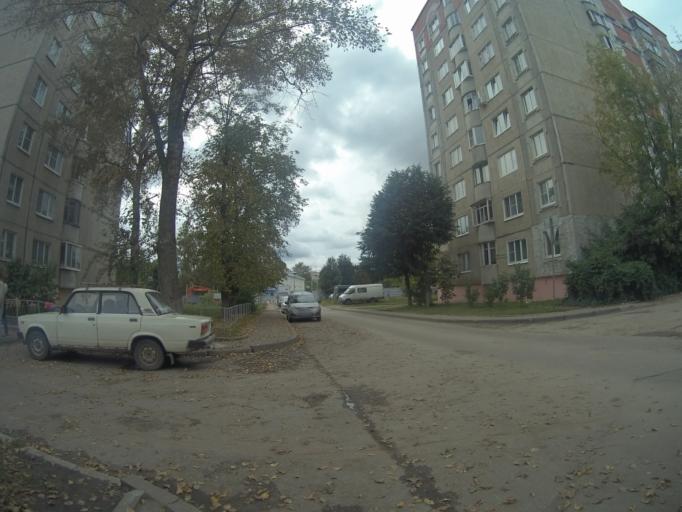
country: RU
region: Vladimir
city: Vladimir
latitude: 56.1154
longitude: 40.3535
